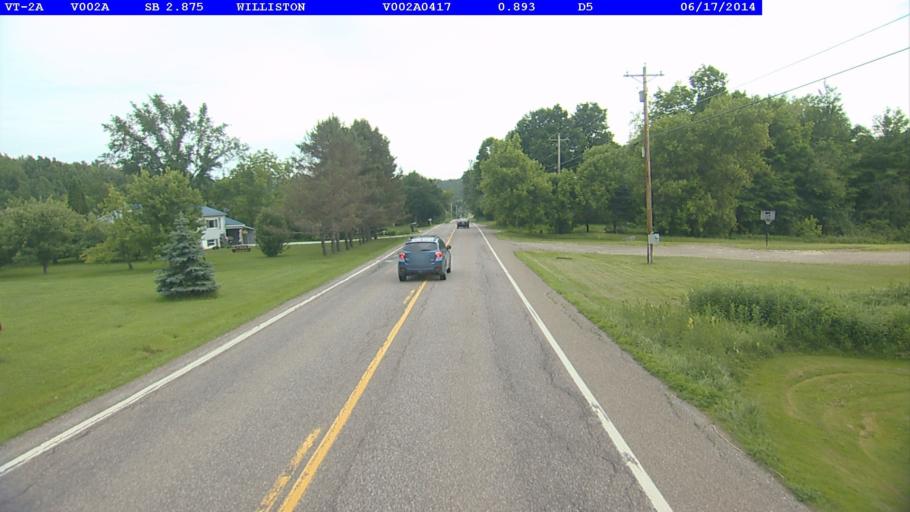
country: US
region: Vermont
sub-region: Chittenden County
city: Williston
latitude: 44.4106
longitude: -73.1249
